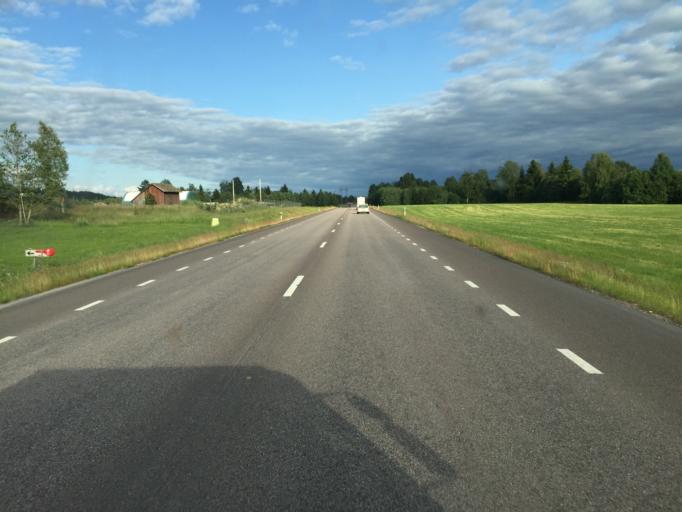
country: SE
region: Dalarna
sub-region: Gagnefs Kommun
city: Djuras
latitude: 60.5544
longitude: 15.1514
